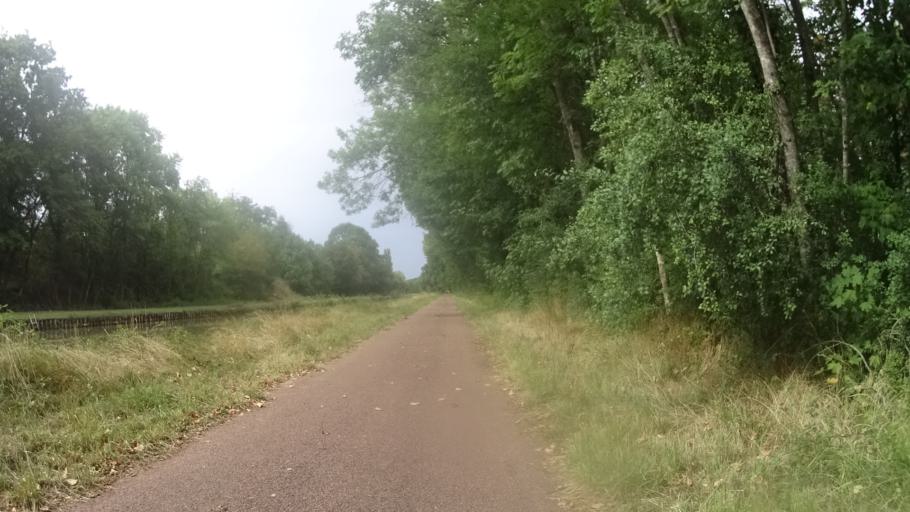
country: FR
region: Bourgogne
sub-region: Departement de la Nievre
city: Imphy
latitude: 46.9182
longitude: 3.2411
